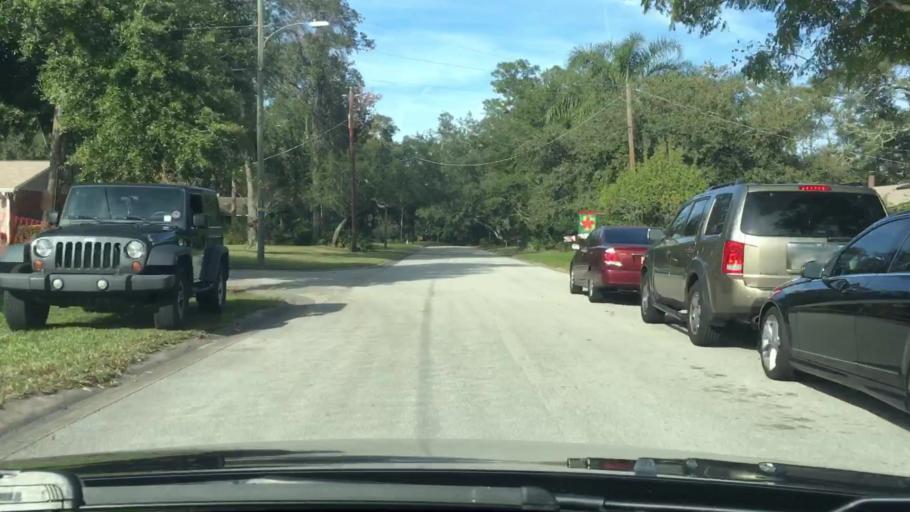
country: US
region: Florida
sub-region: Volusia County
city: Ormond Beach
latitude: 29.2732
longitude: -81.1010
